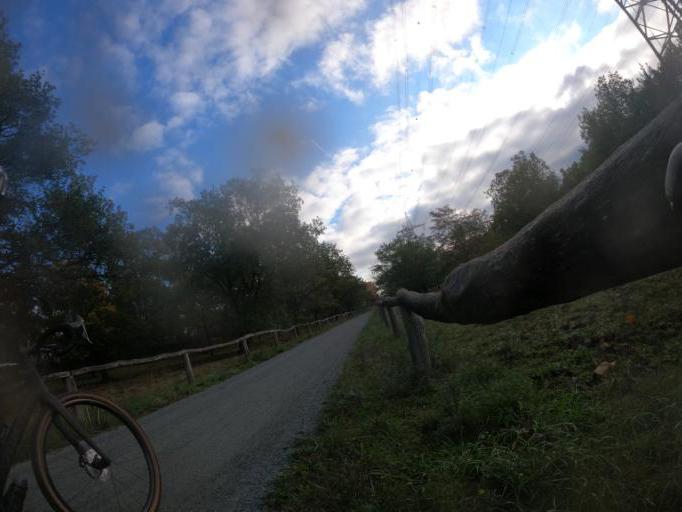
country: DE
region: Hesse
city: Kelsterbach
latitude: 50.0501
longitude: 8.5156
